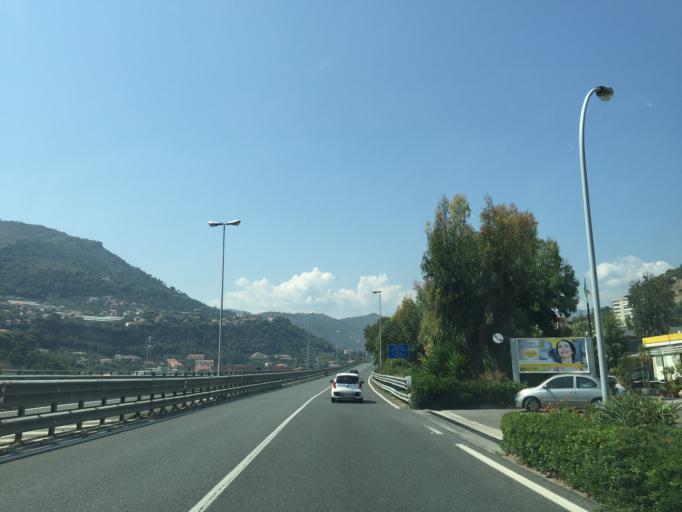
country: IT
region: Liguria
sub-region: Provincia di Imperia
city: Ventimiglia
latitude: 43.8027
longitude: 7.5964
